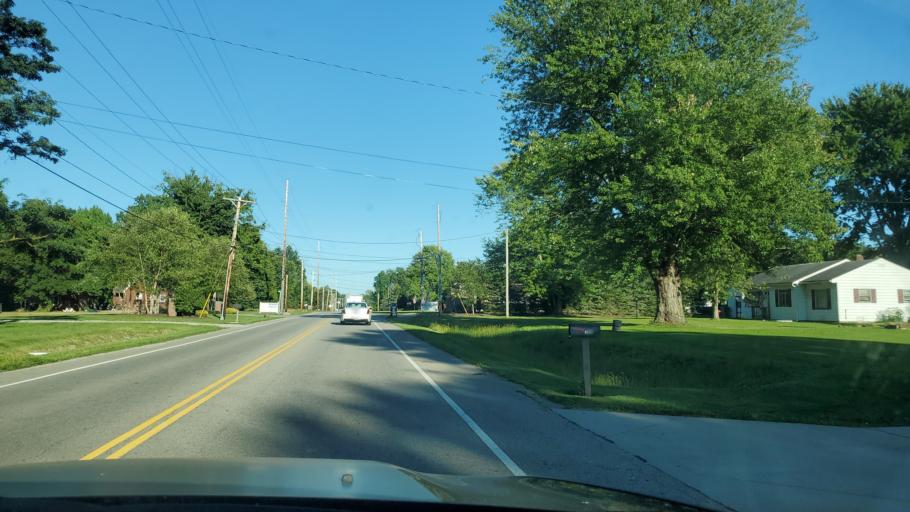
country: US
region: Ohio
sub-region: Mahoning County
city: Boardman
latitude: 40.9880
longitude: -80.6828
